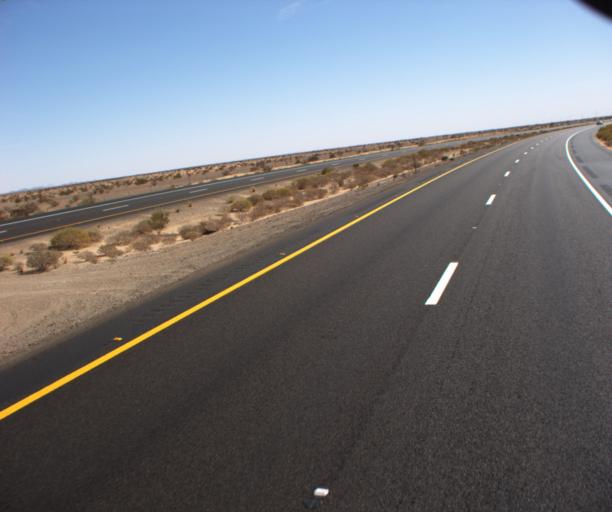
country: US
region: Arizona
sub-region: Yuma County
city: Somerton
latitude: 32.5043
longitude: -114.5585
